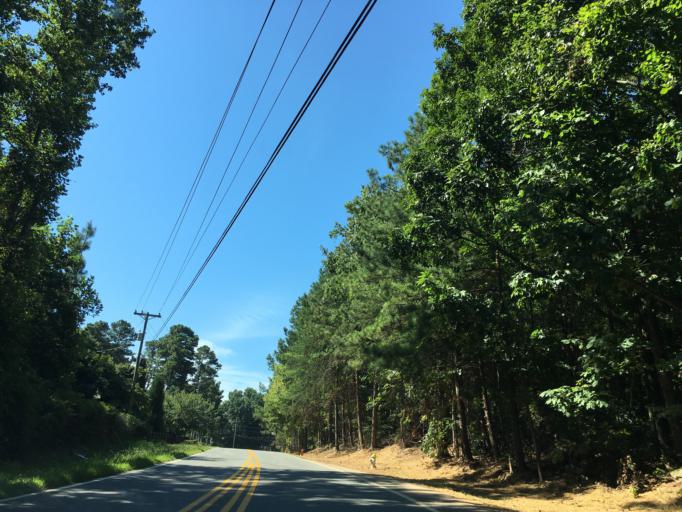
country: US
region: Georgia
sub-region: Fulton County
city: Milton
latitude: 34.1831
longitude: -84.3044
